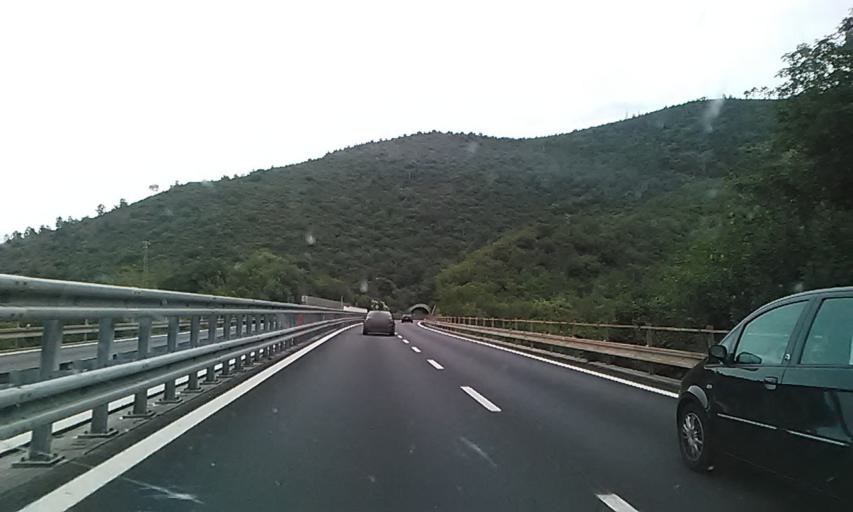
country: IT
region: Liguria
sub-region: Provincia di Savona
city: Borghetto Santo Spirito
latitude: 44.1122
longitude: 8.2302
